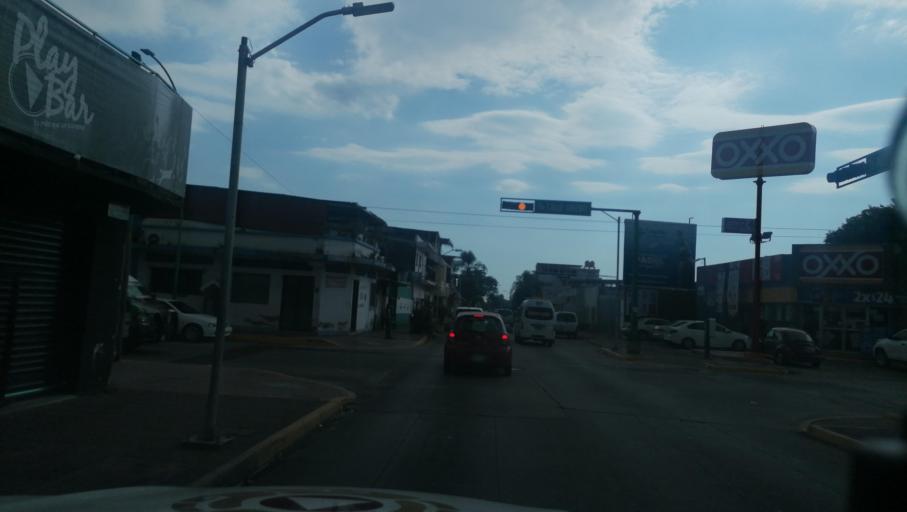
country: MX
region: Chiapas
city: Tapachula
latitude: 14.9091
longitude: -92.2570
